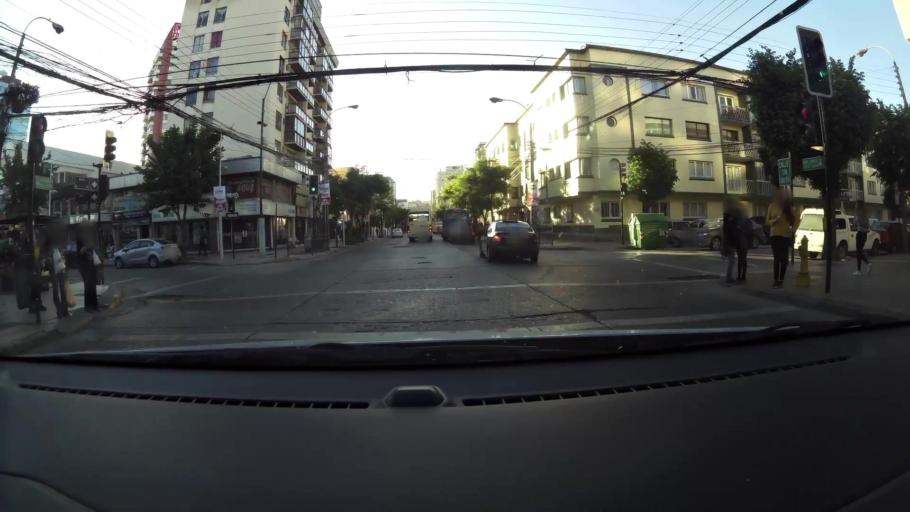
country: CL
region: Valparaiso
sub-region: Provincia de Valparaiso
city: Vina del Mar
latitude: -33.0237
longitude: -71.5538
